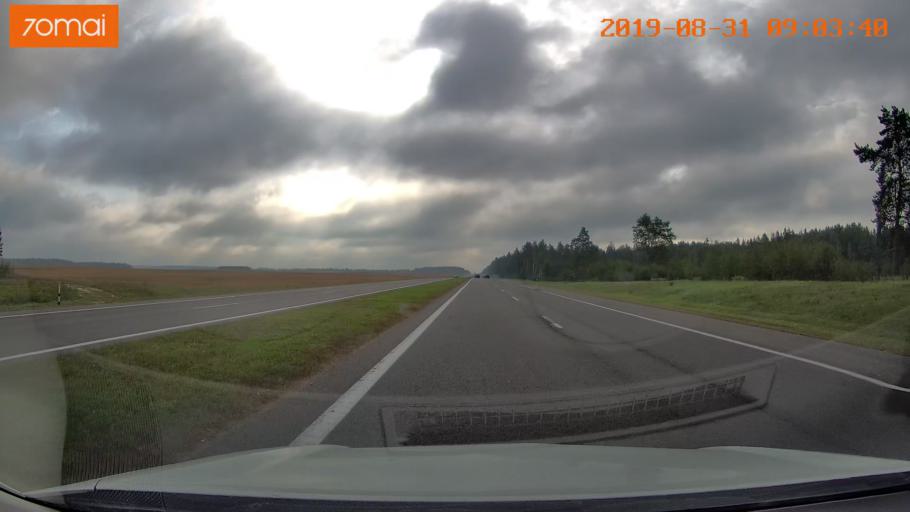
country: BY
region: Minsk
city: Chervyen'
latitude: 53.7389
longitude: 28.3229
